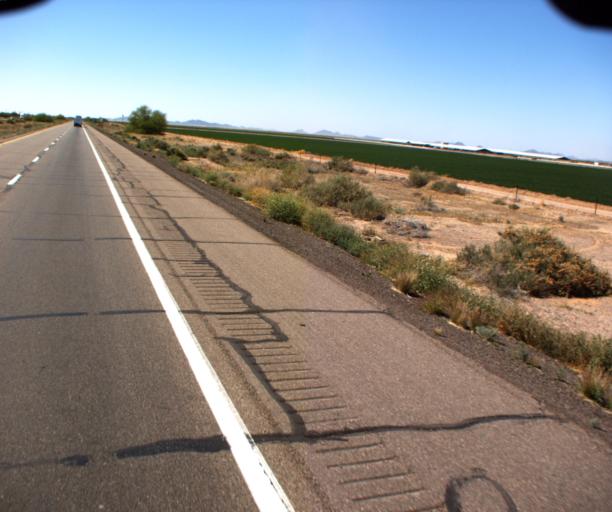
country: US
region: Arizona
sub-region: Maricopa County
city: Gila Bend
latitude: 32.9311
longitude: -112.8144
